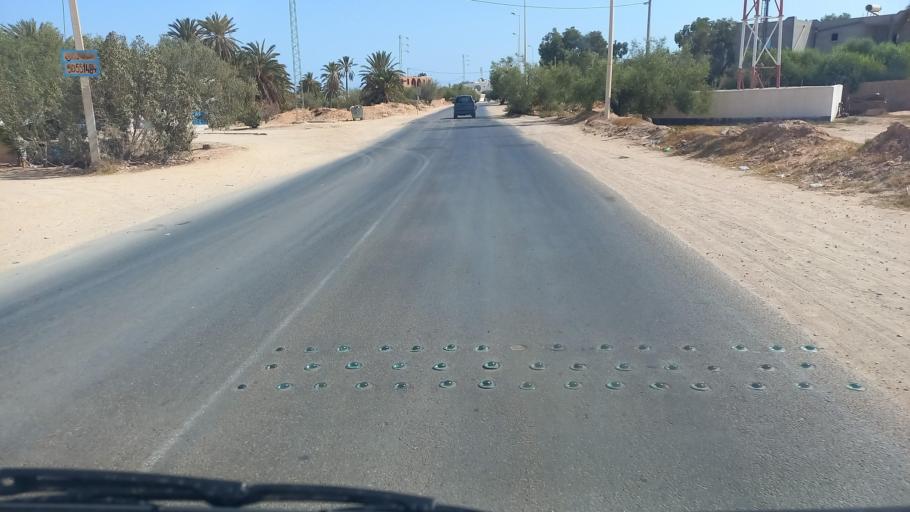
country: TN
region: Madanin
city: Midoun
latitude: 33.7777
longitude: 11.0382
